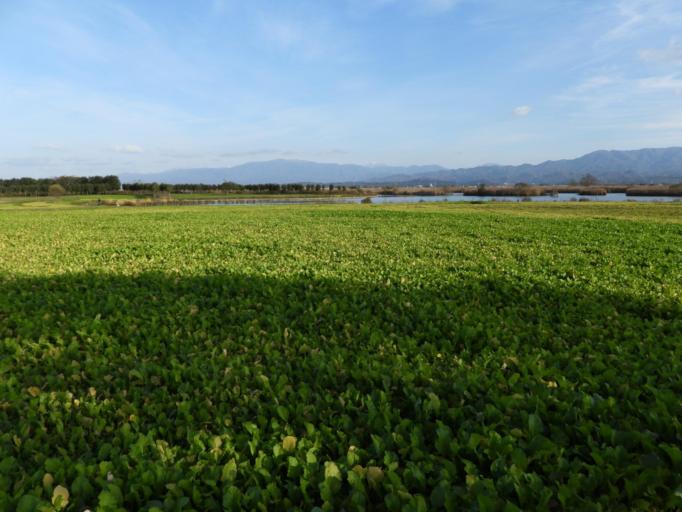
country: JP
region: Niigata
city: Suibara
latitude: 37.9121
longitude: 139.2418
